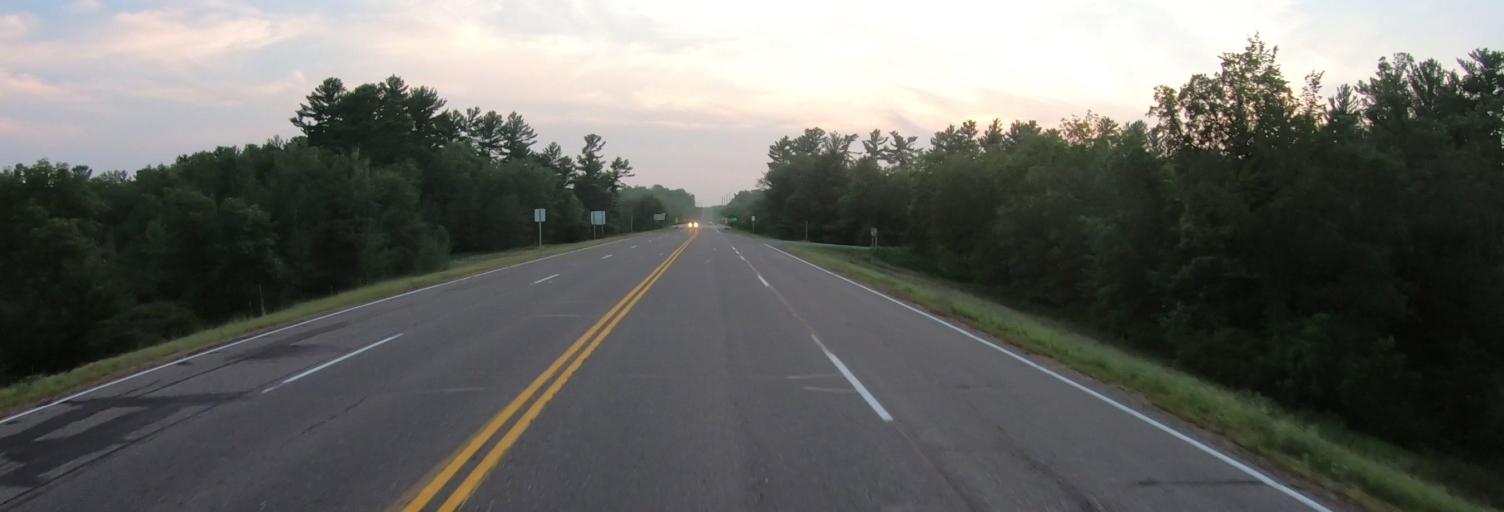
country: US
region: Wisconsin
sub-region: Burnett County
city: Grantsburg
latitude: 45.7733
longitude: -92.7769
